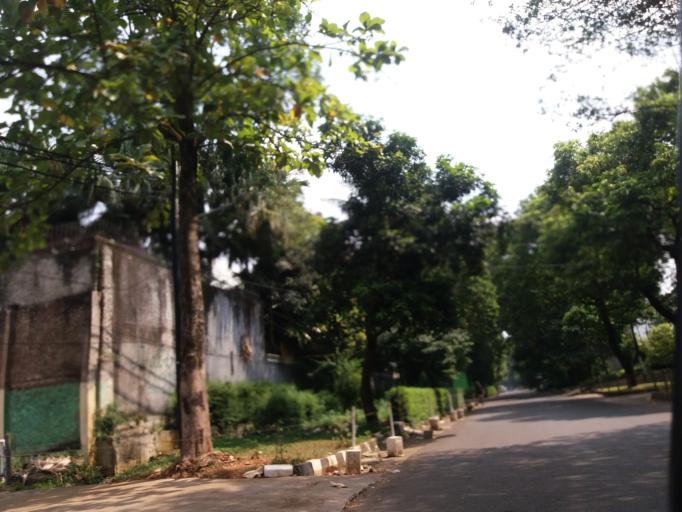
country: ID
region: Jakarta Raya
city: Jakarta
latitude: -6.2326
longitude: 106.8049
